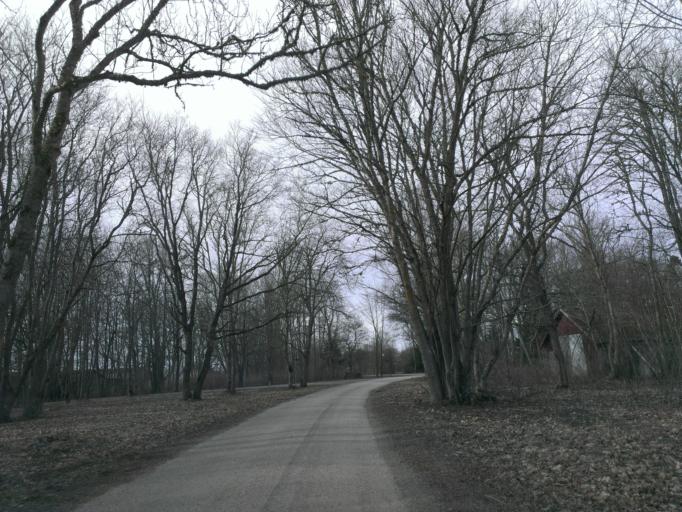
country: EE
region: Laeaene
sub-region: Lihula vald
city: Lihula
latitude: 58.5815
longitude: 23.5382
